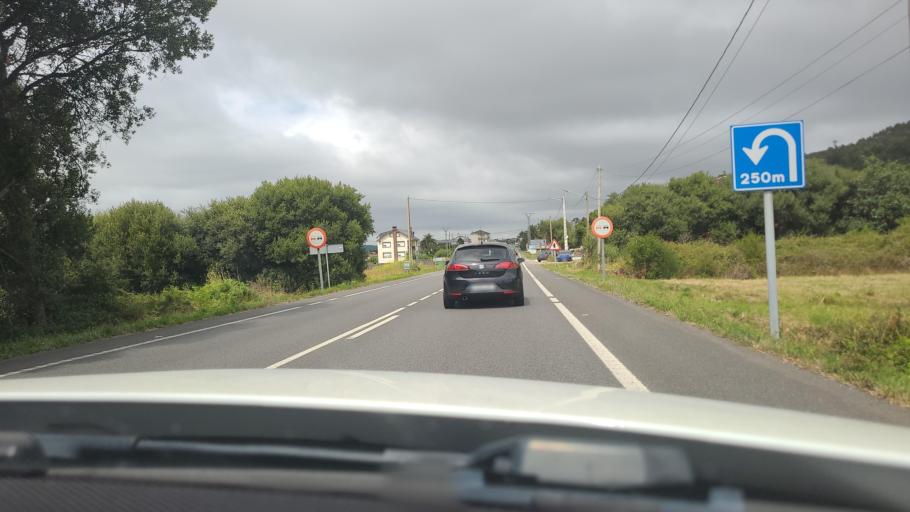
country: ES
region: Galicia
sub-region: Provincia da Coruna
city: Cee
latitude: 42.9843
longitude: -9.1858
